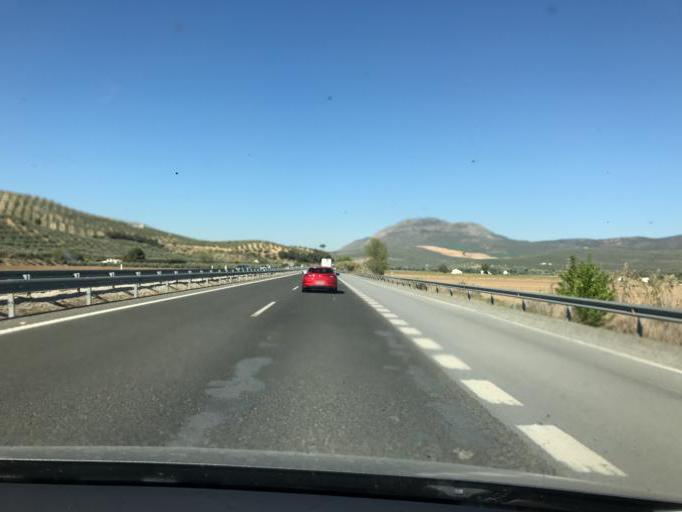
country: ES
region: Andalusia
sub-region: Provincia de Granada
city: Huetor-Tajar
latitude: 37.1804
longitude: -4.0626
